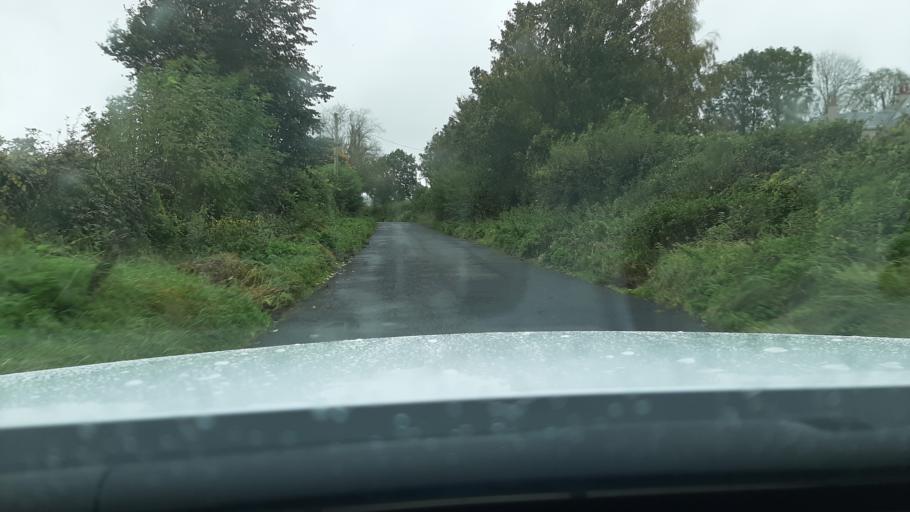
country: IE
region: Leinster
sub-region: Kildare
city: Kildare
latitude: 53.1719
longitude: -6.9212
